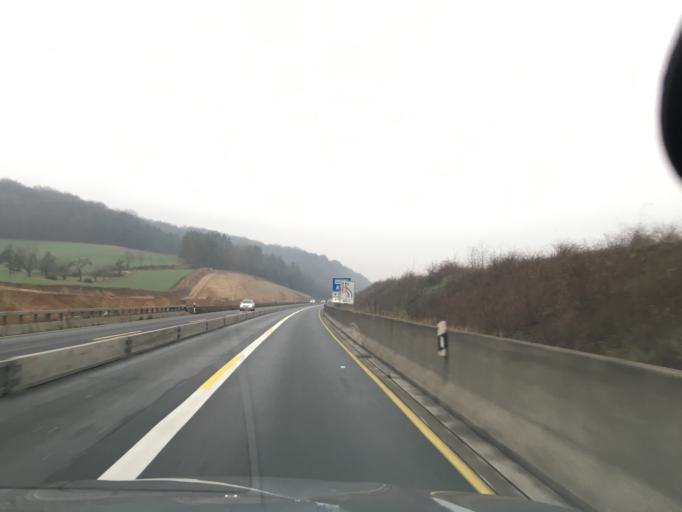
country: DE
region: Bavaria
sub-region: Regierungsbezirk Unterfranken
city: Neubrunn
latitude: 49.7647
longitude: 9.6067
